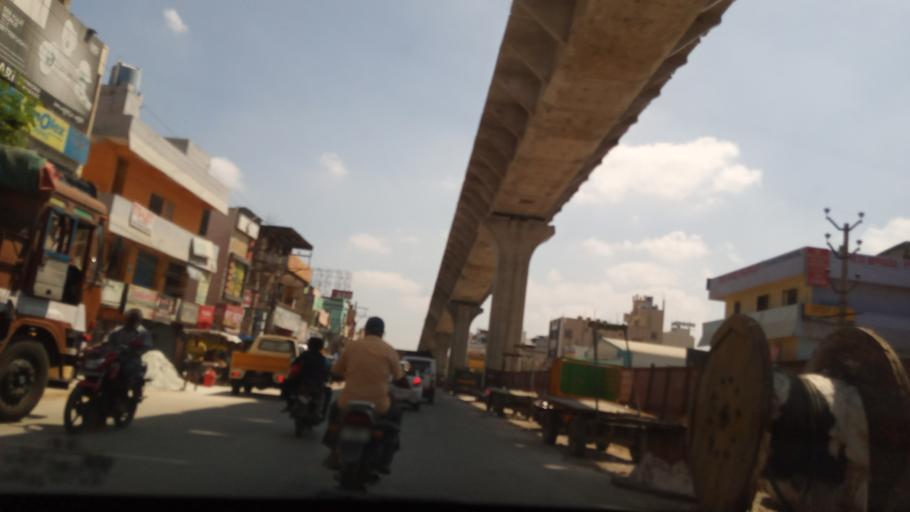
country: IN
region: Andhra Pradesh
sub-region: Chittoor
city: Tirupati
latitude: 13.6424
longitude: 79.4299
